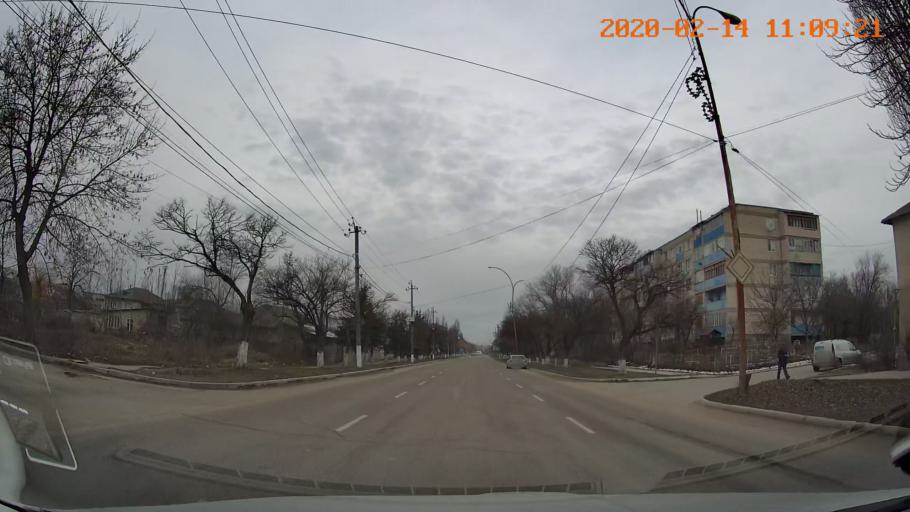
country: MD
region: Raionul Edinet
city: Edinet
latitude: 48.1776
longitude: 27.2948
